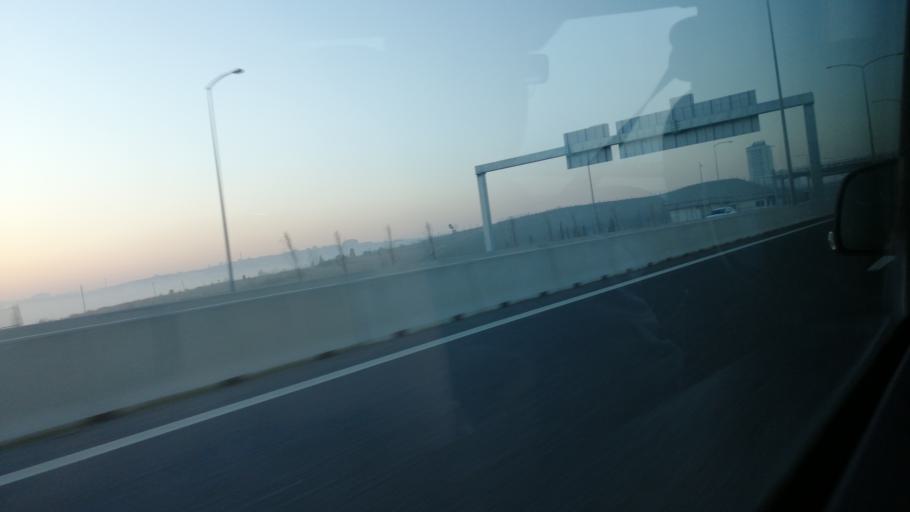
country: TR
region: Kocaeli
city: Tavsanli
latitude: 40.7836
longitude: 29.5164
